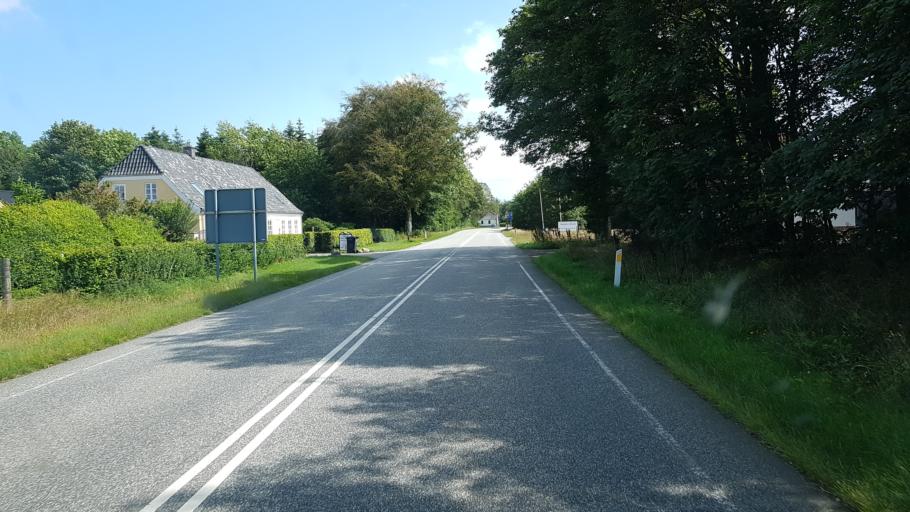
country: DK
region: South Denmark
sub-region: Billund Kommune
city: Billund
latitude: 55.6673
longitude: 9.1981
